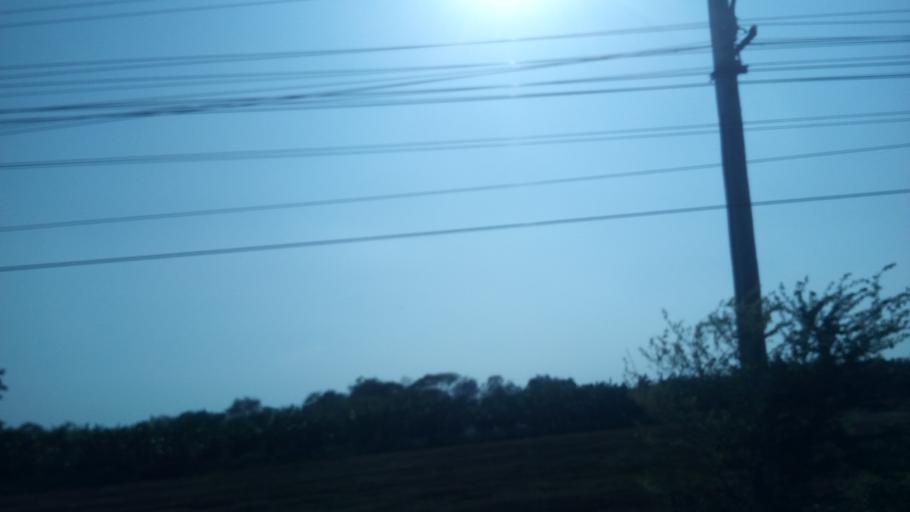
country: TH
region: Nonthaburi
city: Sai Noi
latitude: 13.9279
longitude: 100.3190
